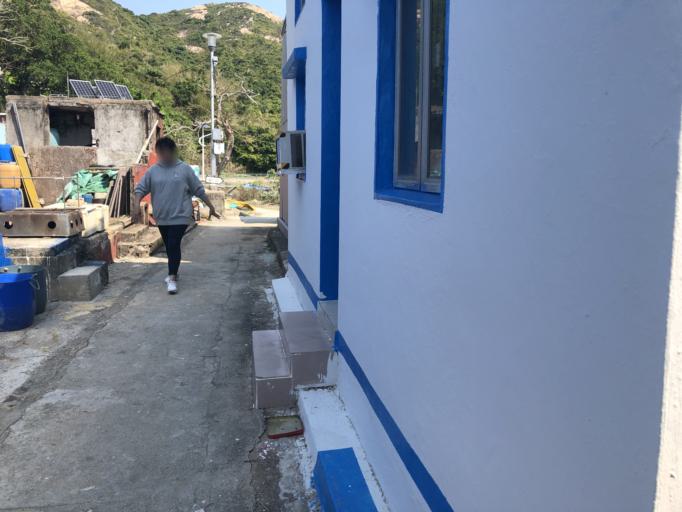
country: HK
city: Sok Kwu Wan
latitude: 22.1650
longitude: 114.2543
